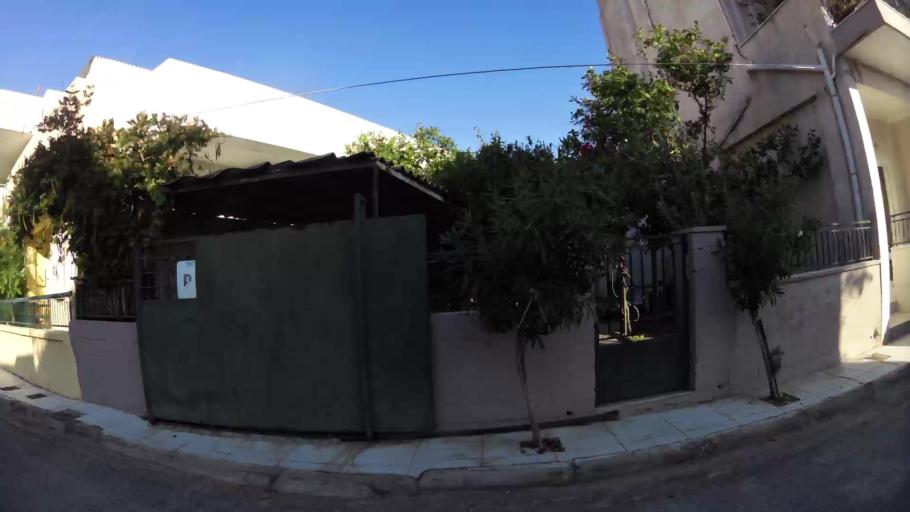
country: GR
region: Attica
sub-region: Nomos Piraios
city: Korydallos
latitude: 37.9758
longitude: 23.6322
